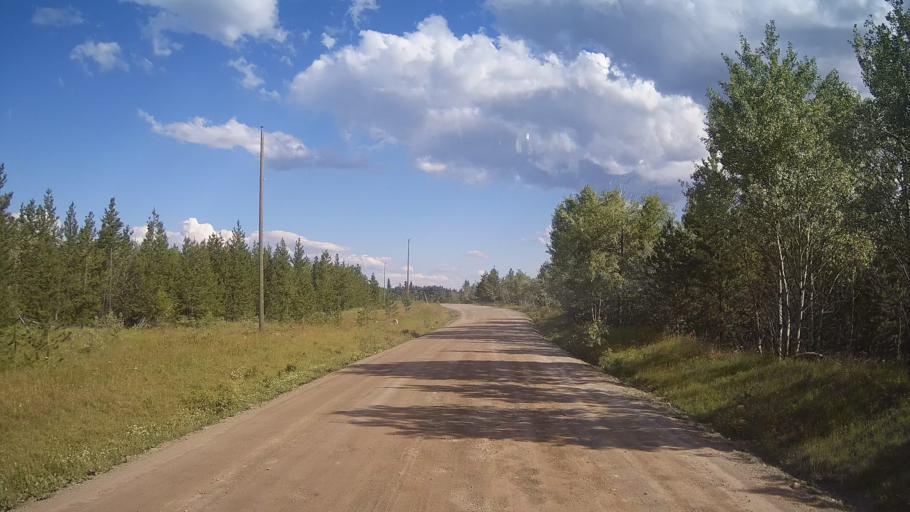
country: CA
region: British Columbia
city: Cache Creek
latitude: 51.2793
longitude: -121.7352
